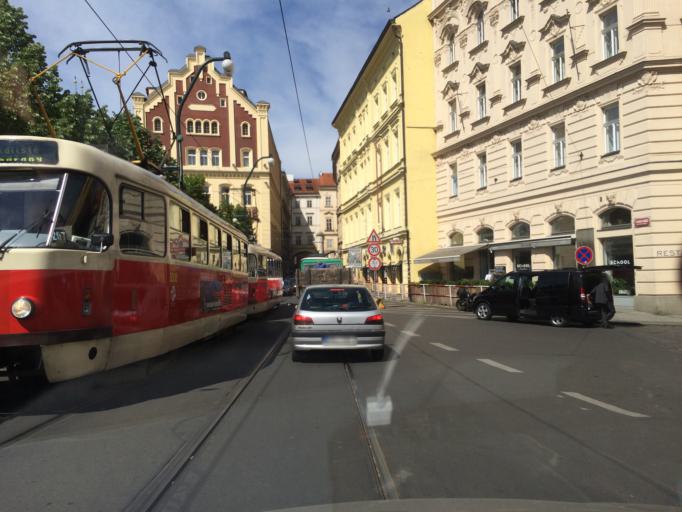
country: CZ
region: Praha
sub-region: Praha 1
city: Stare Mesto
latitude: 50.0848
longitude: 14.4137
